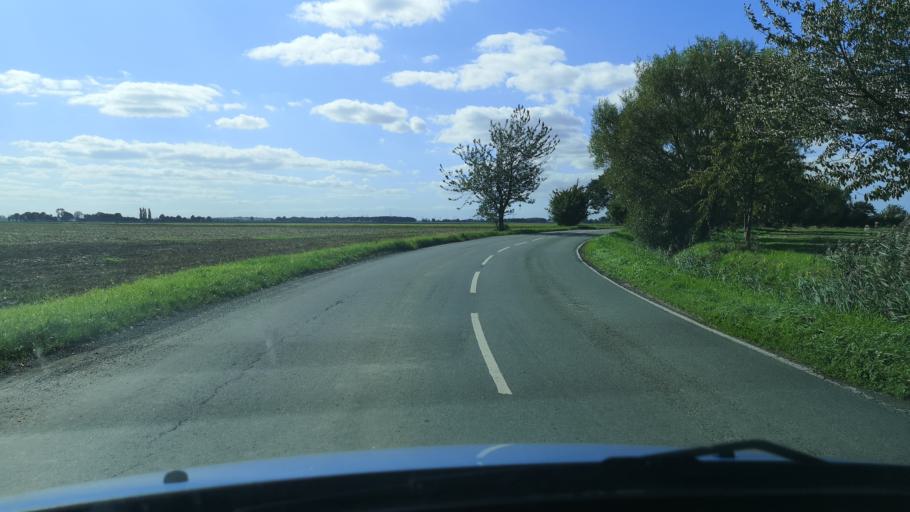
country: GB
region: England
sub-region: North Lincolnshire
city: Eastoft
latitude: 53.6305
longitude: -0.7560
